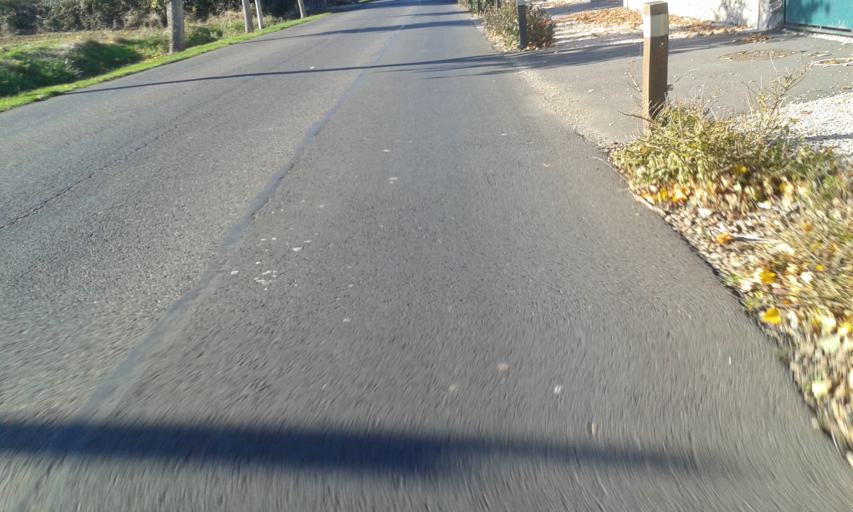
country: FR
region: Centre
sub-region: Departement du Loir-et-Cher
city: Oucques
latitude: 47.8272
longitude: 1.3885
